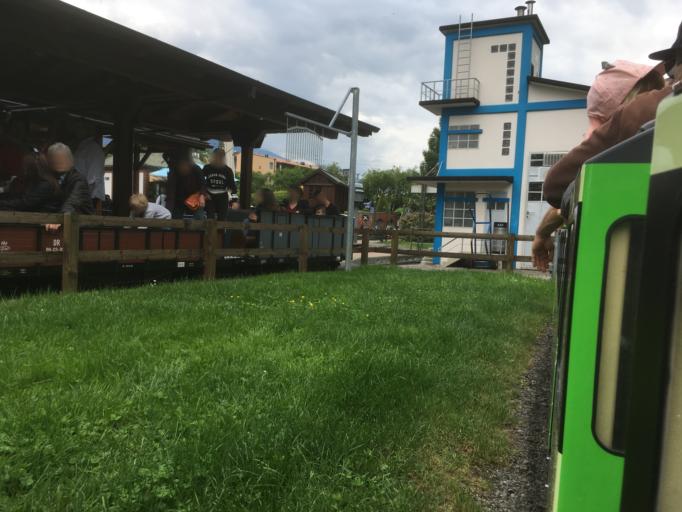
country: CH
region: Valais
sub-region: Monthey District
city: Port-Valais
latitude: 46.3847
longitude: 6.8569
